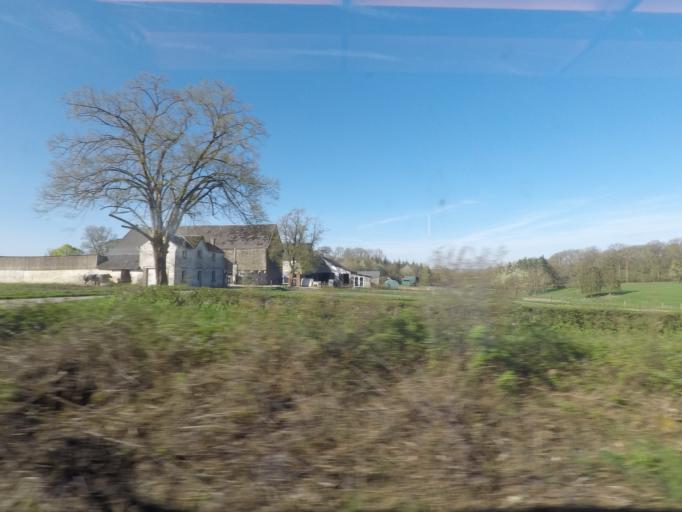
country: BE
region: Wallonia
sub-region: Province de Namur
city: Hamois
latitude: 50.2626
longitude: 5.1801
